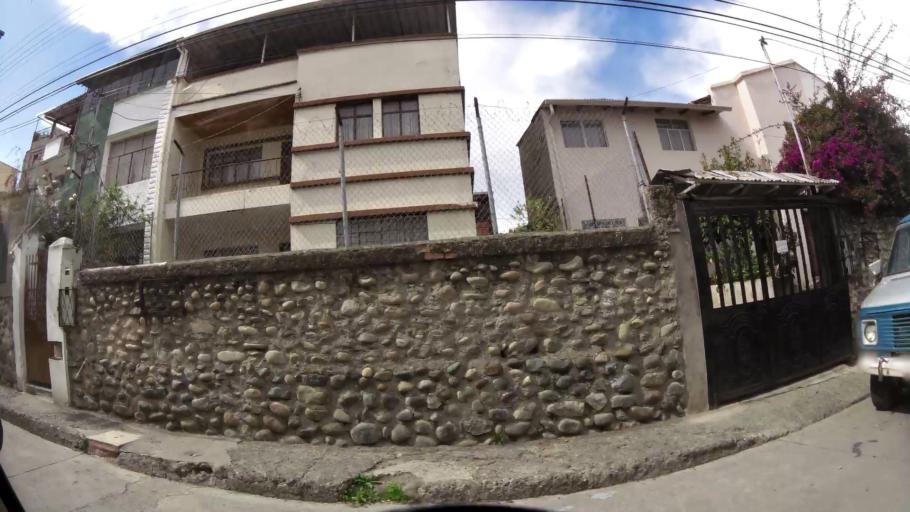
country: EC
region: Azuay
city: Cuenca
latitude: -2.8899
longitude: -78.9969
